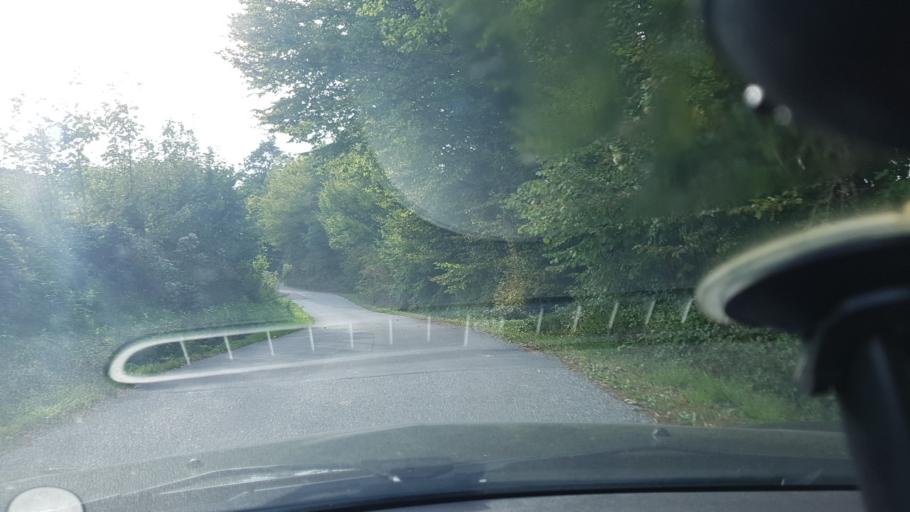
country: HR
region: Krapinsko-Zagorska
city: Radoboj
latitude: 46.1775
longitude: 15.9634
